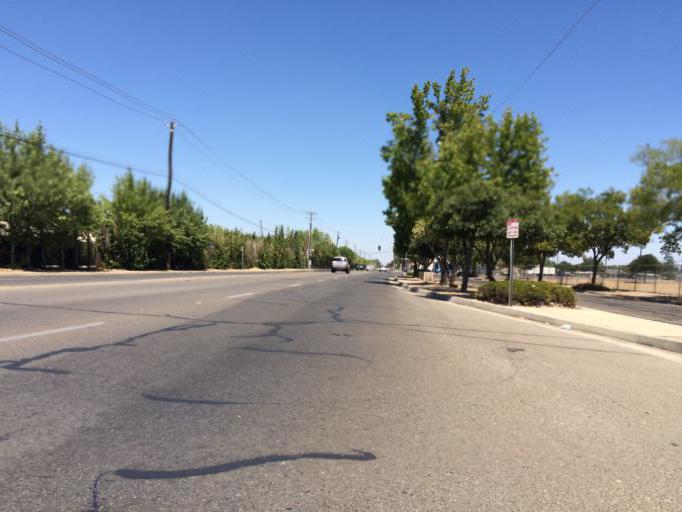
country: US
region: California
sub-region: Fresno County
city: Fresno
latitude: 36.7272
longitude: -119.7456
